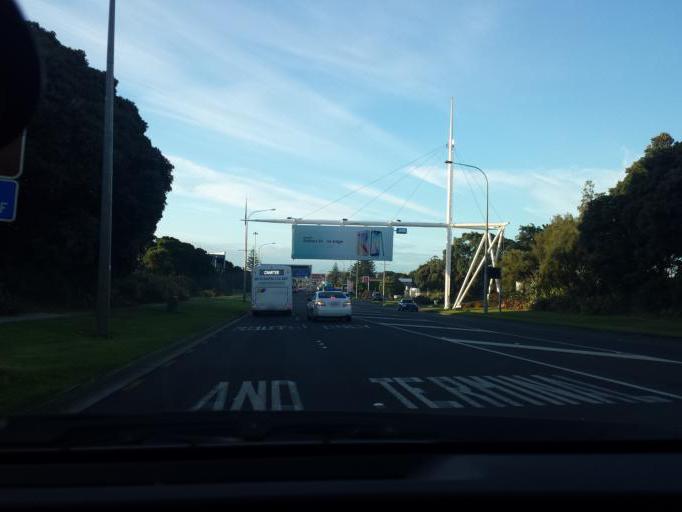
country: NZ
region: Auckland
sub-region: Auckland
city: Mangere
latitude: -36.9993
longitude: 174.7880
